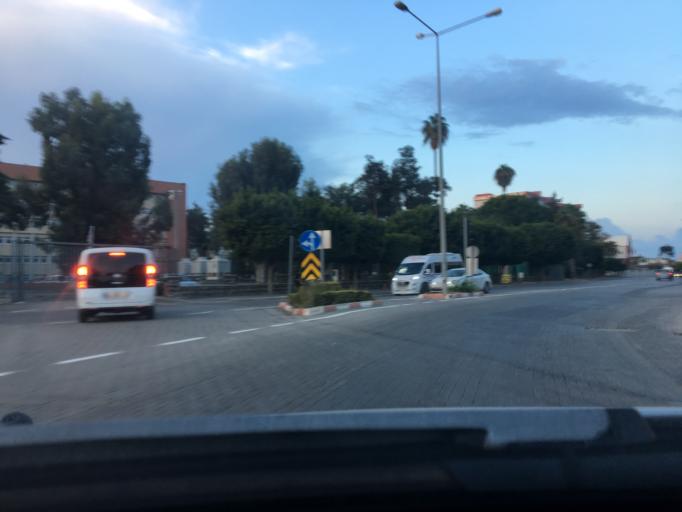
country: TR
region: Adana
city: Adana
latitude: 37.0016
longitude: 35.3133
